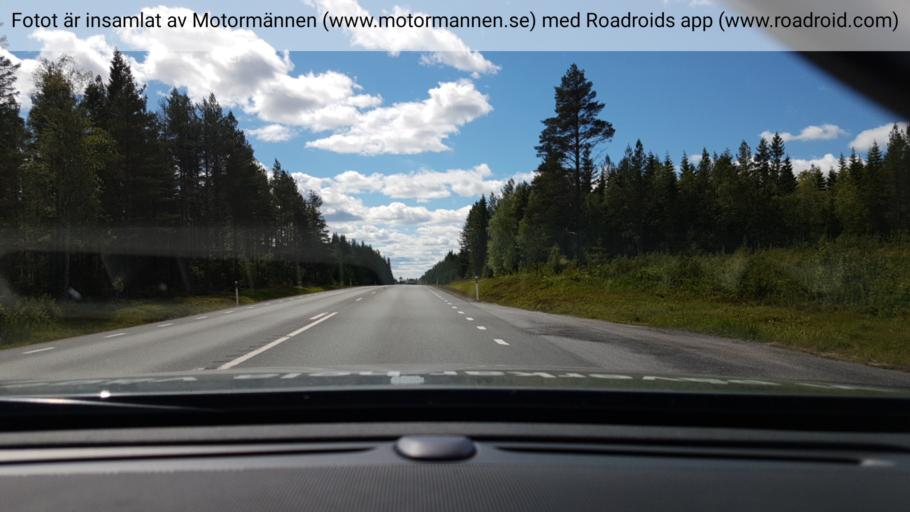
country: SE
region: Vaesterbotten
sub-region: Skelleftea Kommun
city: Burea
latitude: 64.3448
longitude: 21.2850
